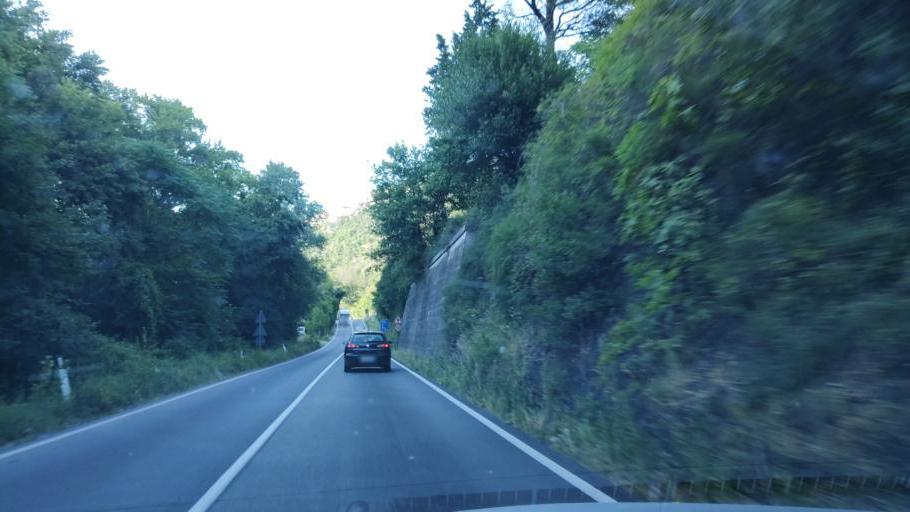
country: IT
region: Umbria
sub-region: Provincia di Terni
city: Narni
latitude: 42.5086
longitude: 12.5143
